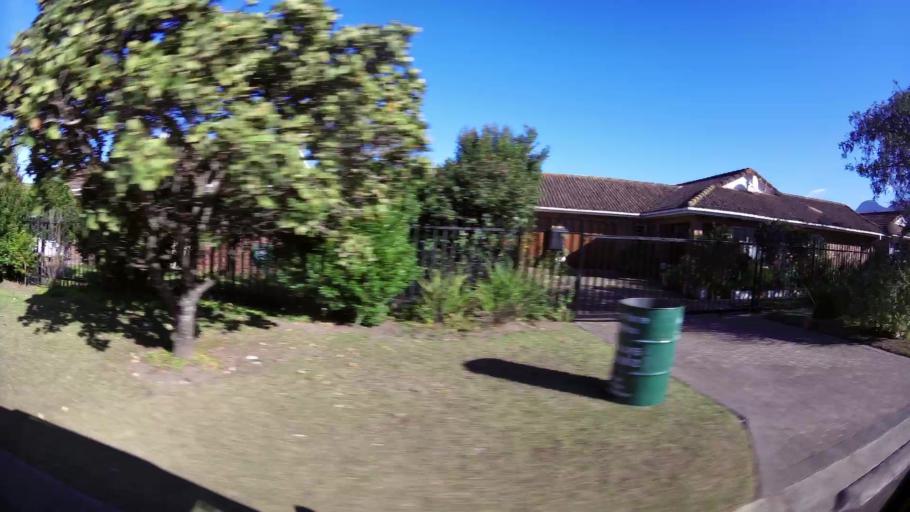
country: ZA
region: Western Cape
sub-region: Eden District Municipality
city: George
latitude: -33.9599
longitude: 22.4244
